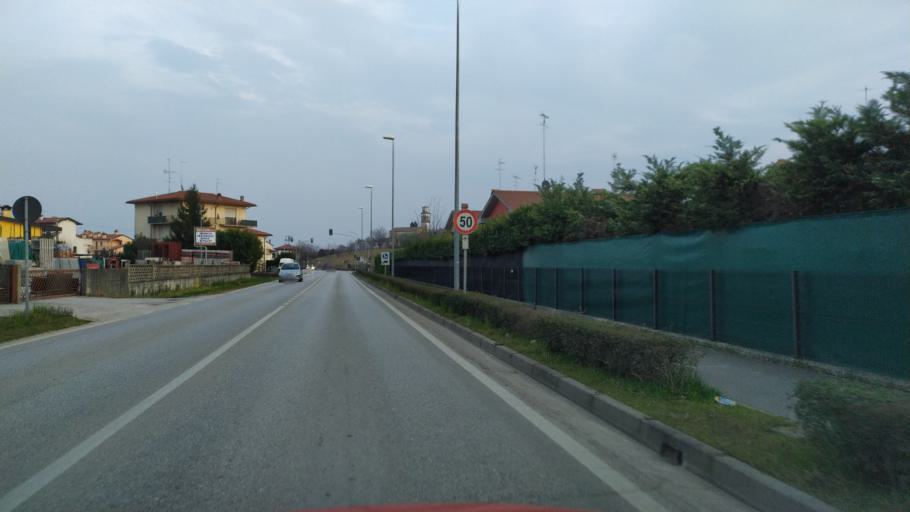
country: IT
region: Veneto
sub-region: Provincia di Vicenza
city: Preara-Moraro-Leva Nord
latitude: 45.6761
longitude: 11.5526
